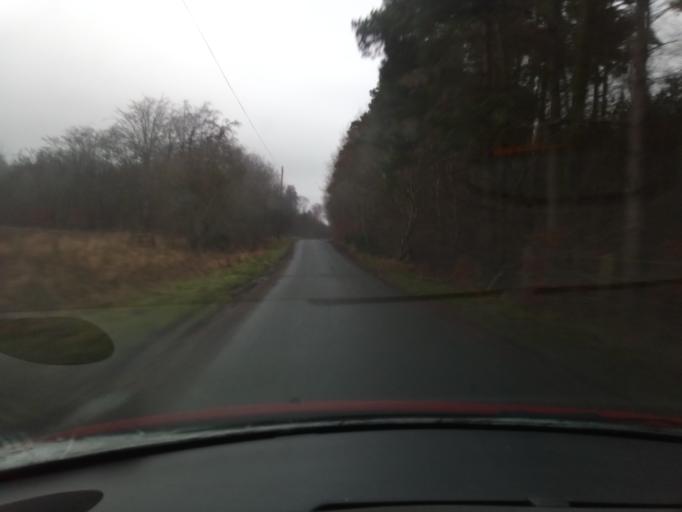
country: GB
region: Scotland
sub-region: The Scottish Borders
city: Kelso
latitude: 55.5536
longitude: -2.4311
